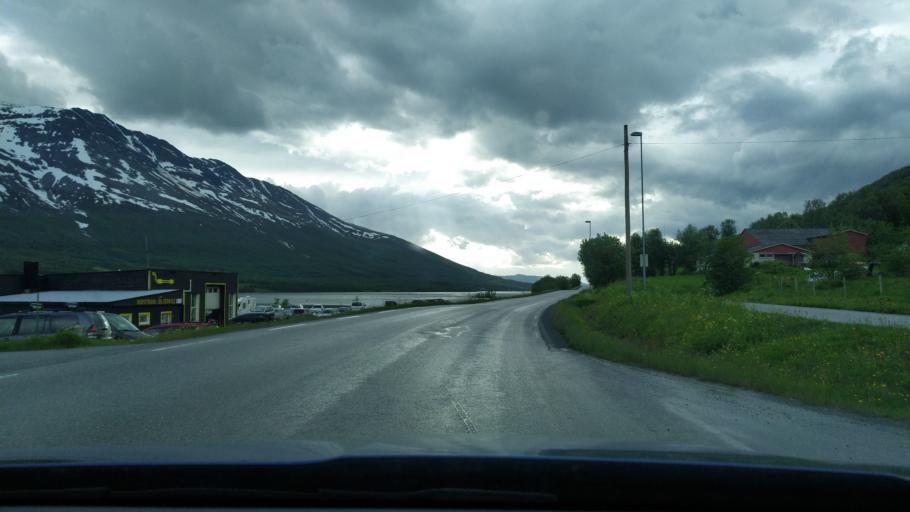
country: NO
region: Troms
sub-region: Balsfjord
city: Storsteinnes
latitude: 69.2202
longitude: 19.5381
